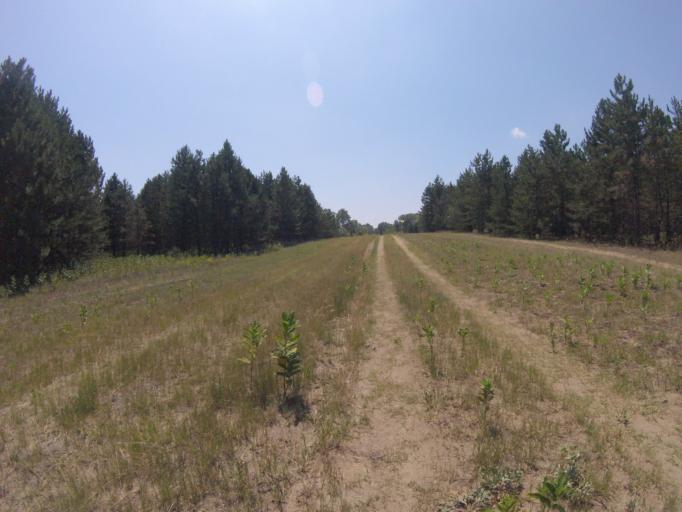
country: HU
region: Bacs-Kiskun
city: Jaszszentlaszlo
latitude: 46.6117
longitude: 19.7096
